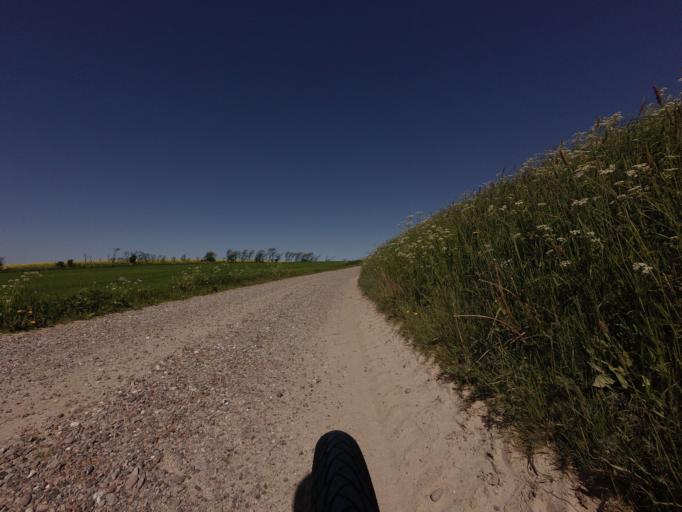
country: DK
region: North Denmark
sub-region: Hjorring Kommune
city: Hjorring
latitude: 57.4480
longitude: 9.8991
